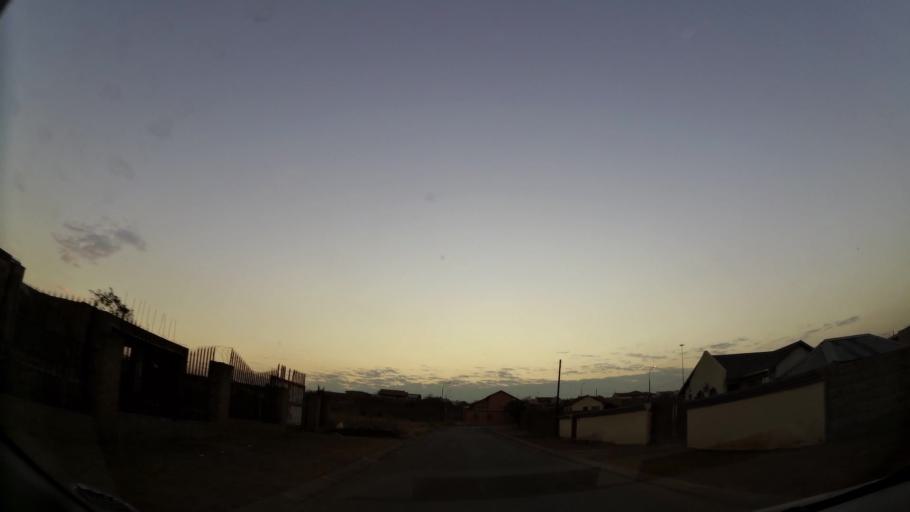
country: ZA
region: Gauteng
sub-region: West Rand District Municipality
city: Randfontein
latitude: -26.2125
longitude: 27.7111
